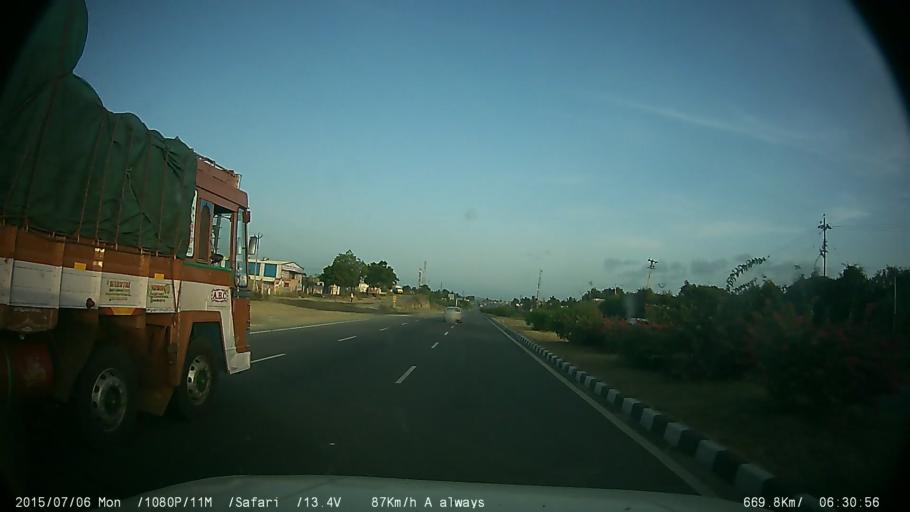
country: IN
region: Tamil Nadu
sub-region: Krishnagiri
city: Kelamangalam
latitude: 12.6804
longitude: 77.9460
